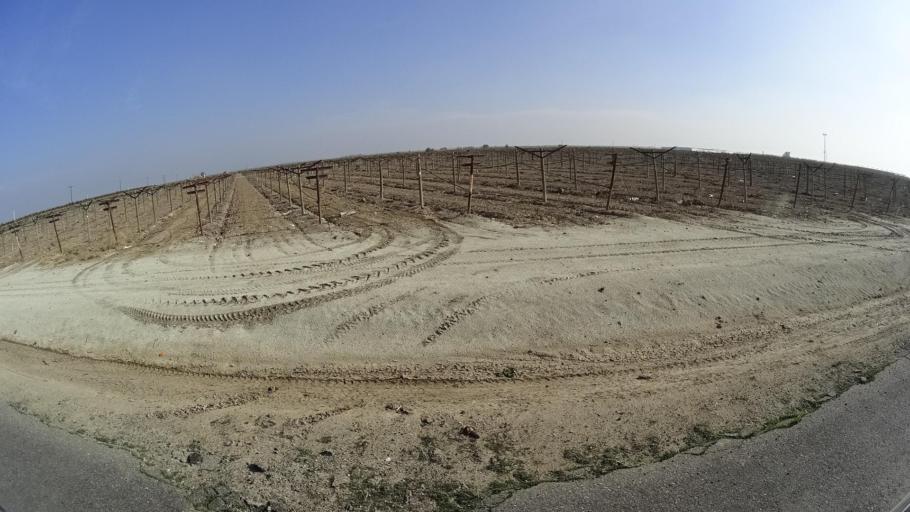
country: US
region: California
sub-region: Tulare County
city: Richgrove
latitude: 35.7243
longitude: -119.1557
